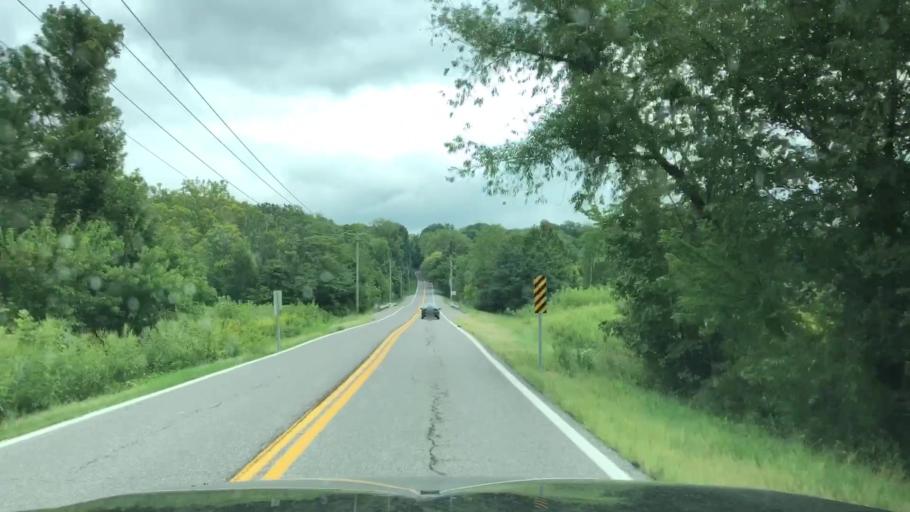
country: US
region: Missouri
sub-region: Saint Louis County
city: Hazelwood
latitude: 38.8112
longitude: -90.3933
